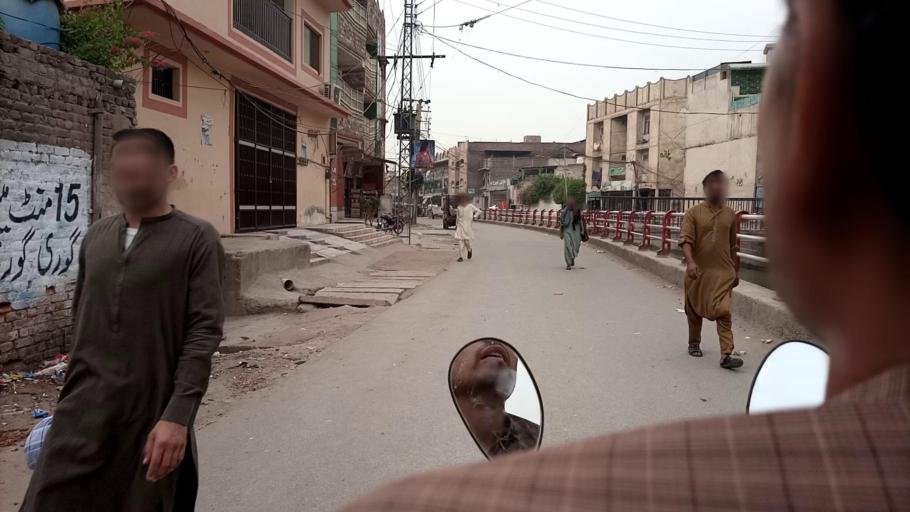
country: PK
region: Khyber Pakhtunkhwa
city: Peshawar
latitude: 34.0211
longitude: 71.5924
